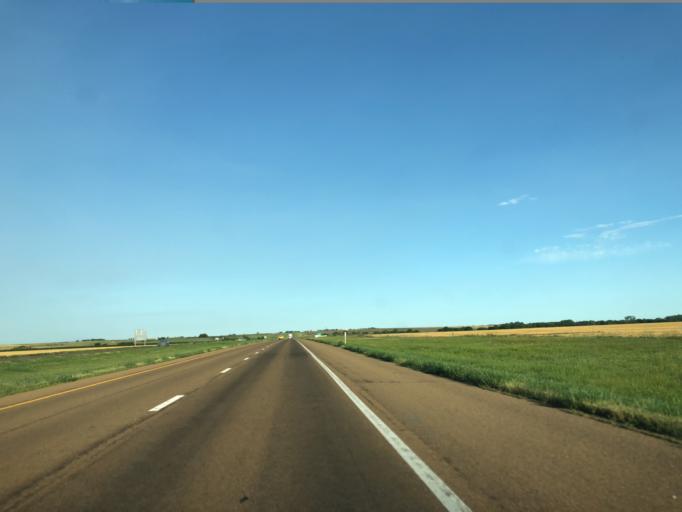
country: US
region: Kansas
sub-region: Ellis County
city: Victoria
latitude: 38.8638
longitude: -99.0348
